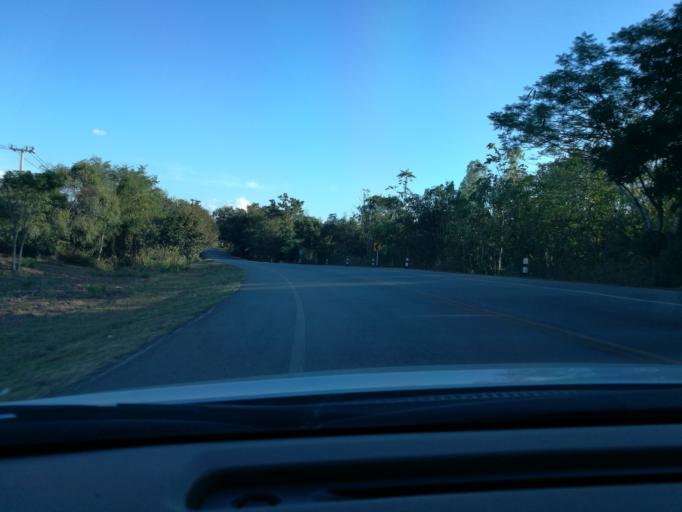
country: TH
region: Phitsanulok
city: Nakhon Thai
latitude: 17.0445
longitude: 100.8094
